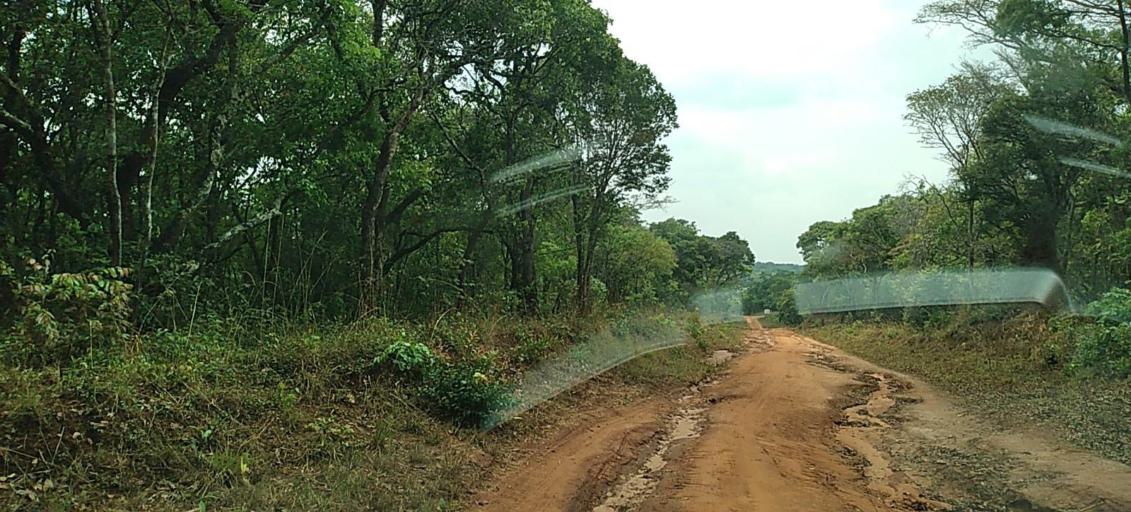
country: ZM
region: North-Western
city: Mwinilunga
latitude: -11.5401
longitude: 24.7815
